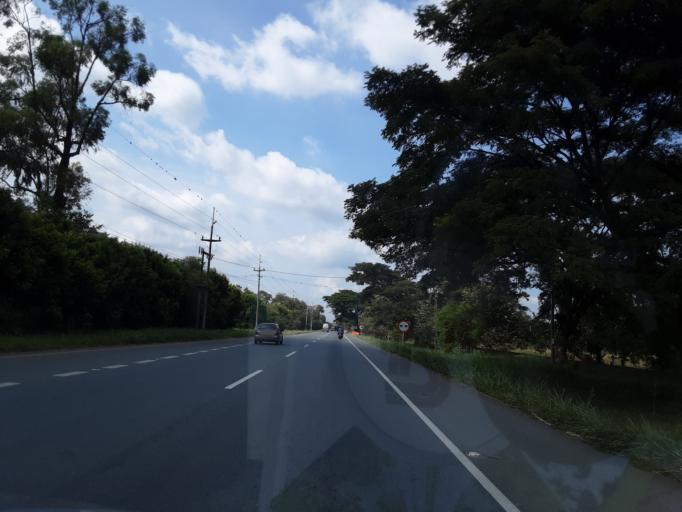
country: CO
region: Valle del Cauca
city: Guacari
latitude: 3.7373
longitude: -76.3239
